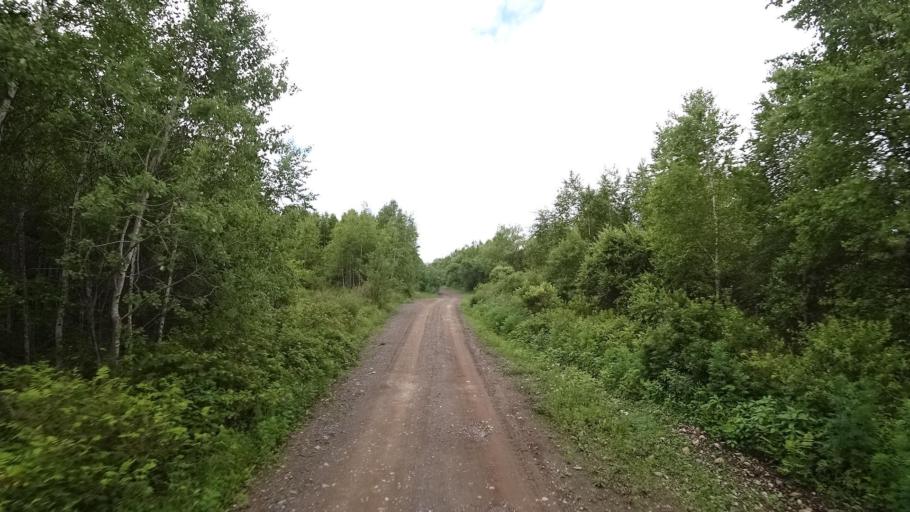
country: RU
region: Khabarovsk Krai
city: Amursk
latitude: 49.9143
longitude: 136.1596
